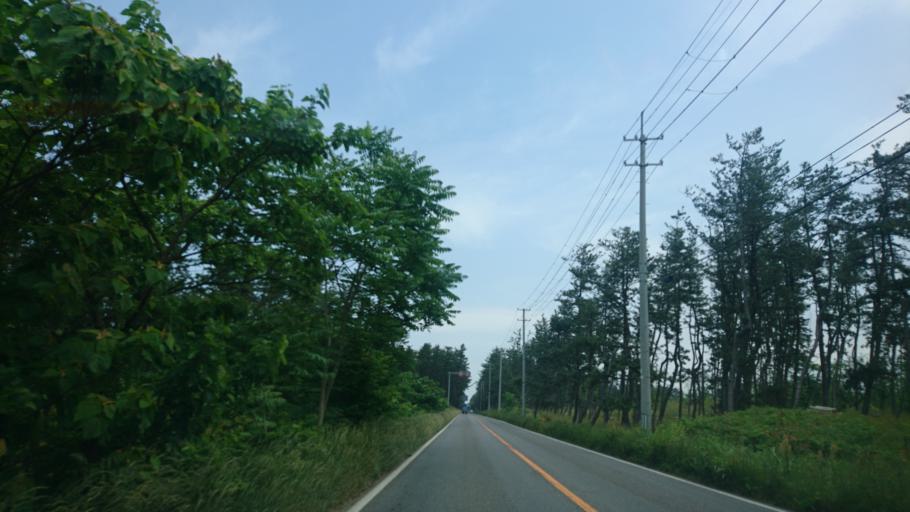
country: JP
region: Niigata
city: Shibata
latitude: 38.0296
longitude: 139.2903
